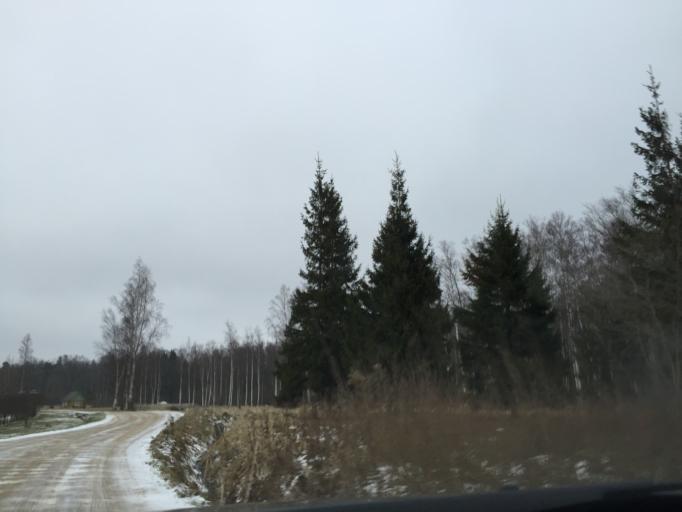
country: LV
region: Salacgrivas
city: Salacgriva
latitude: 57.5099
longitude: 24.3820
